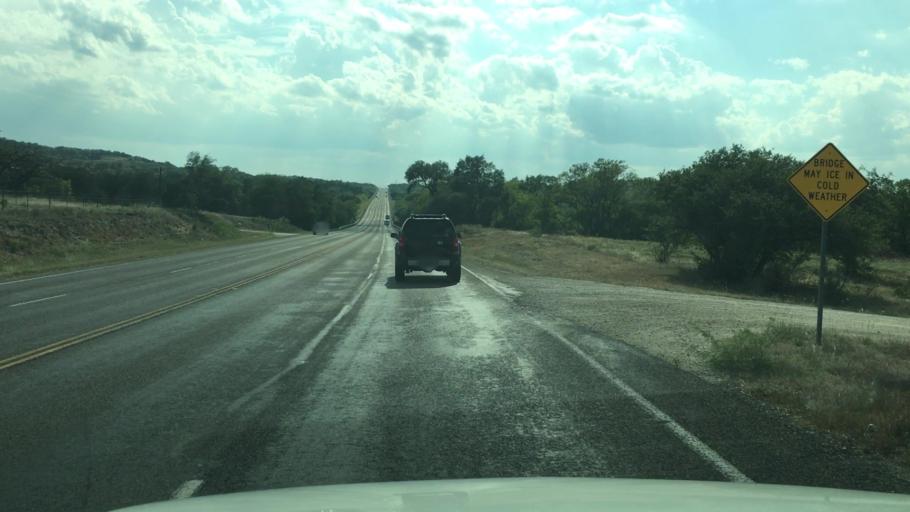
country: US
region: Texas
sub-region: Blanco County
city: Johnson City
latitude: 30.2111
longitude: -98.2819
